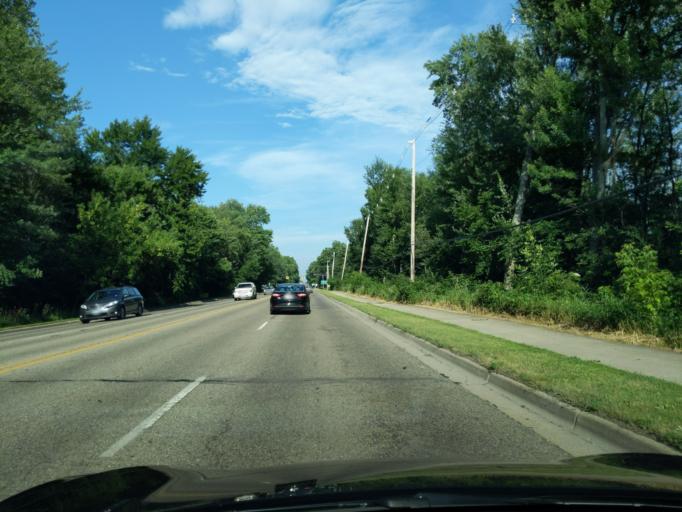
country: US
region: Michigan
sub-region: Ingham County
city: Okemos
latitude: 42.7469
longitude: -84.4504
